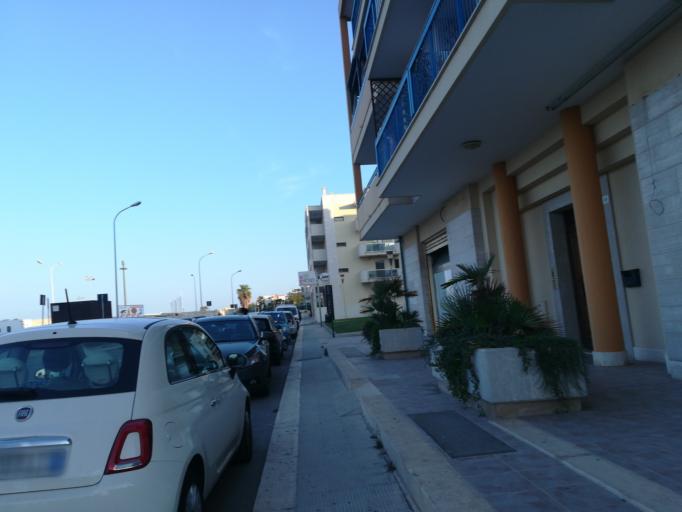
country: IT
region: Apulia
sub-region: Provincia di Bari
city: Polignano a Mare
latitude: 40.9928
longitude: 17.2295
